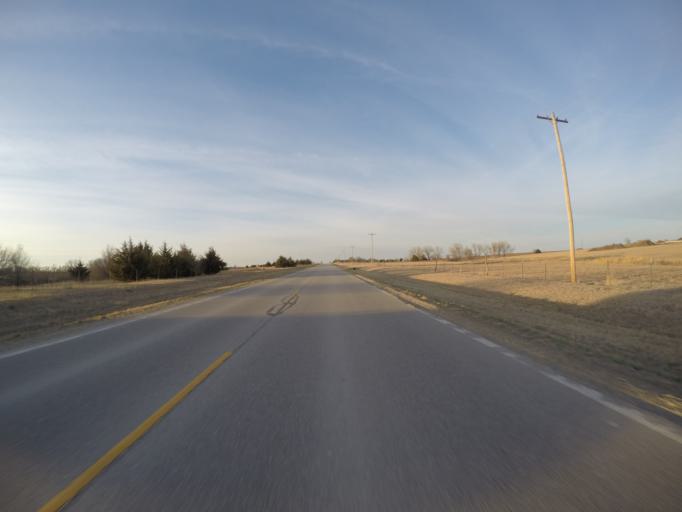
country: US
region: Kansas
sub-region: Riley County
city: Fort Riley North
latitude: 39.3254
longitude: -96.8307
